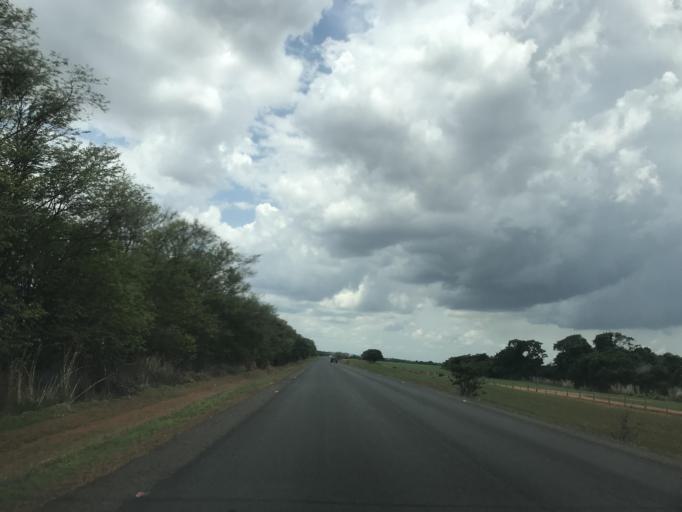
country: BR
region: Goias
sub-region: Vianopolis
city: Vianopolis
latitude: -16.7961
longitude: -48.5204
